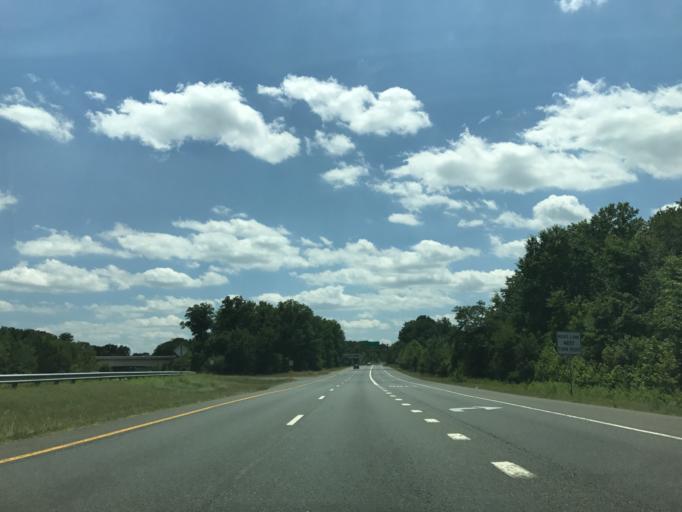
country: US
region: Maryland
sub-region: Prince George's County
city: South Laurel
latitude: 39.0608
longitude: -76.8395
